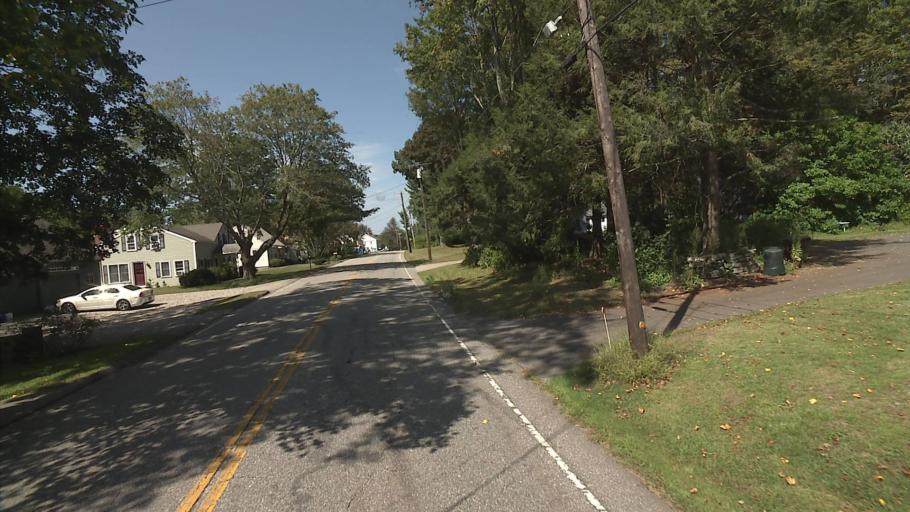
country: US
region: Connecticut
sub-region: Windham County
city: Willimantic
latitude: 41.6640
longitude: -72.2537
